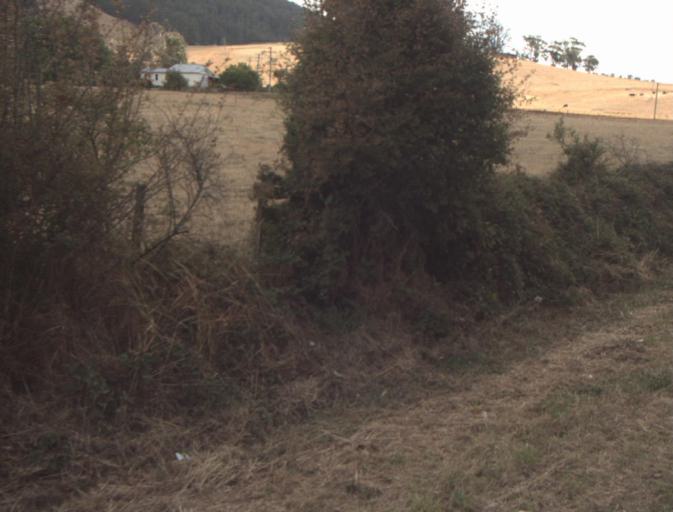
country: AU
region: Tasmania
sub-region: Launceston
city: Mayfield
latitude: -41.2300
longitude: 147.1239
